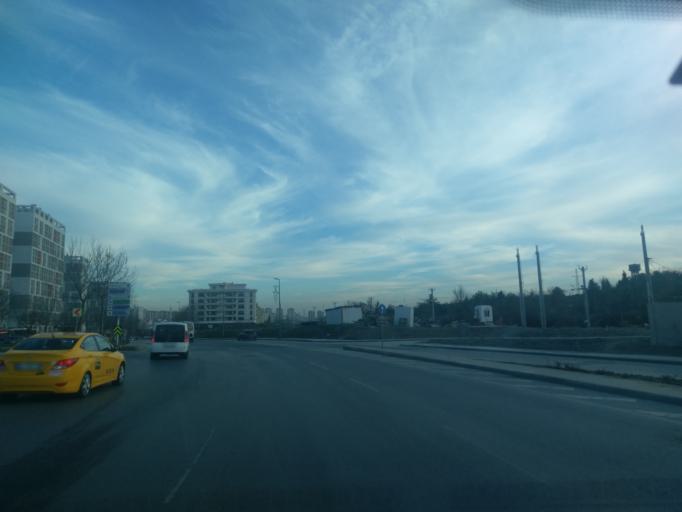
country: TR
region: Istanbul
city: Basaksehir
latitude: 41.0411
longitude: 28.7596
